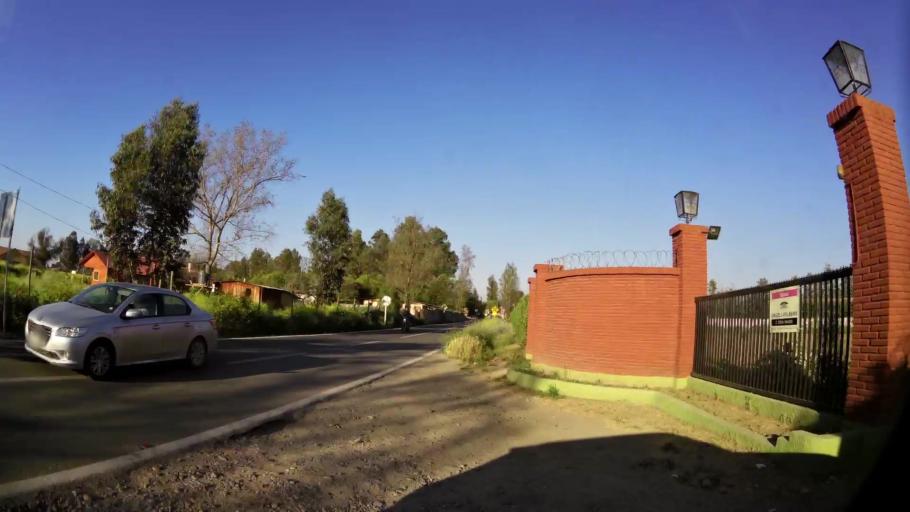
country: CL
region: Santiago Metropolitan
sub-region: Provincia de Talagante
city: Penaflor
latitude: -33.6206
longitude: -70.8704
